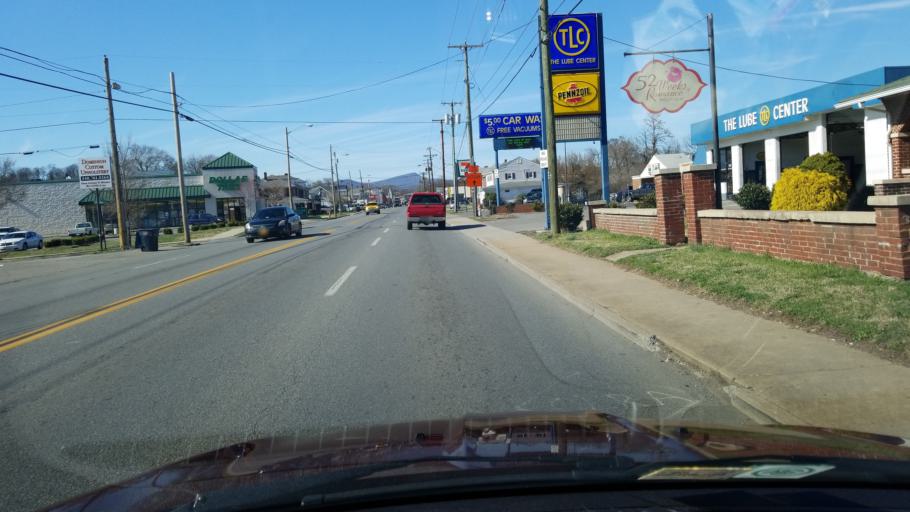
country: US
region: Virginia
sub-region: City of Roanoke
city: Roanoke
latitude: 37.2978
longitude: -79.9389
